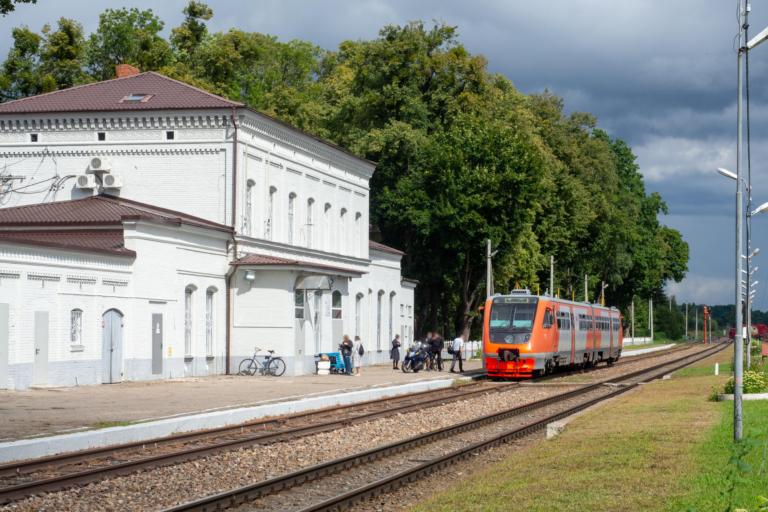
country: RU
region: Kaliningrad
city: Zheleznodorozhnyy
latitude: 54.3565
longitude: 21.3238
